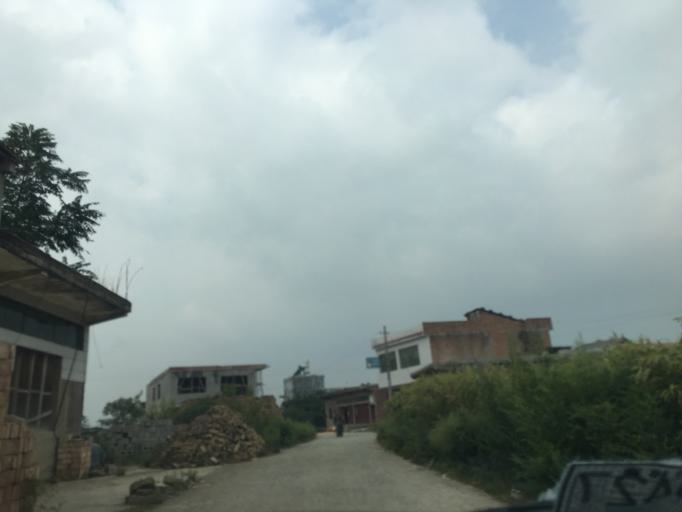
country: CN
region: Guangxi Zhuangzu Zizhiqu
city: Xinzhou
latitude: 25.5705
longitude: 105.6178
